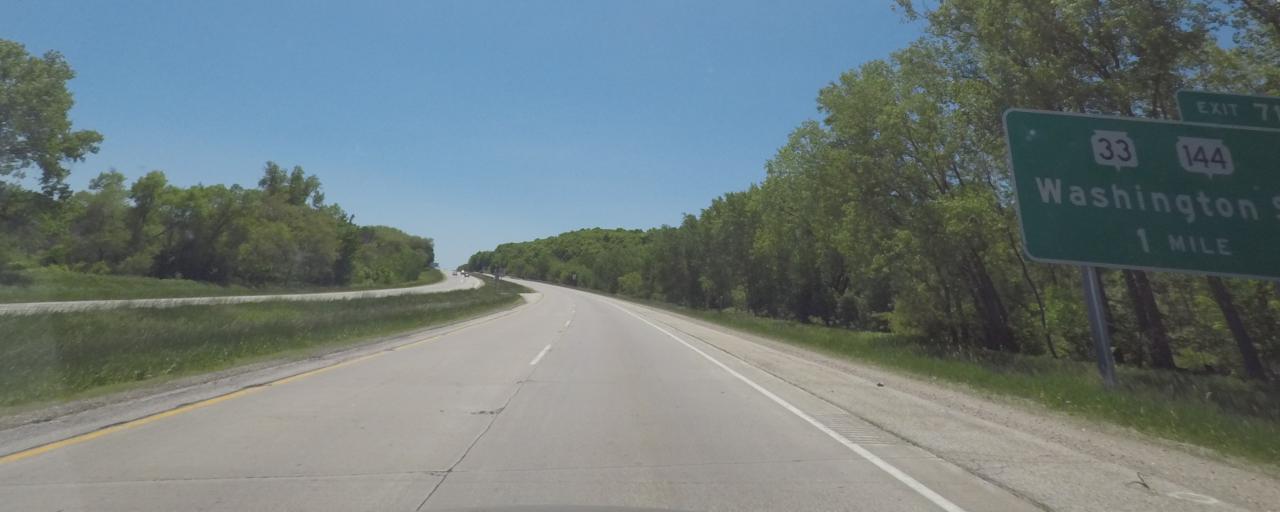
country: US
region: Wisconsin
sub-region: Washington County
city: West Bend
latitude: 43.4472
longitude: -88.2102
